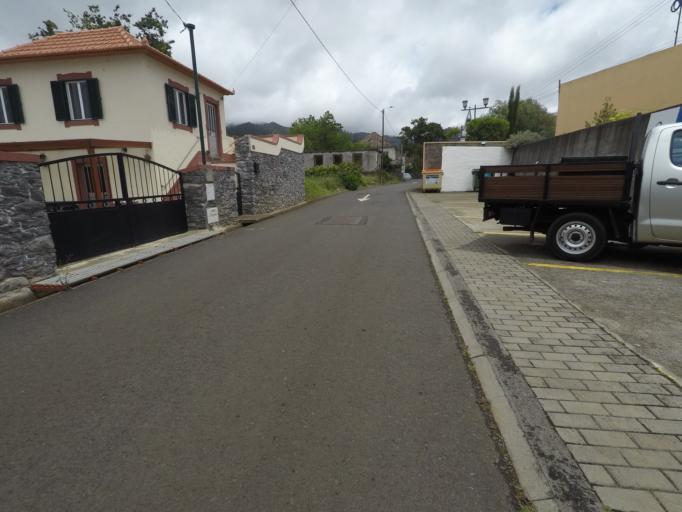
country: PT
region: Madeira
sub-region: Calheta
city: Estreito da Calheta
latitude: 32.7538
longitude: -17.2040
